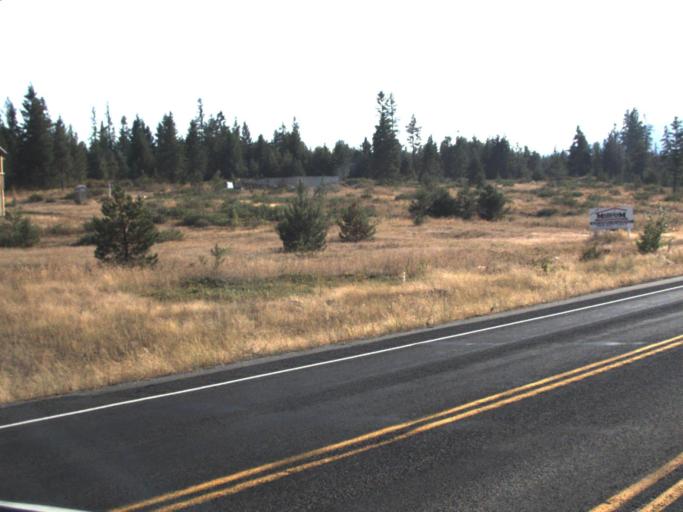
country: US
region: Washington
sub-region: Pend Oreille County
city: Newport
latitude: 48.1130
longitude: -117.2203
